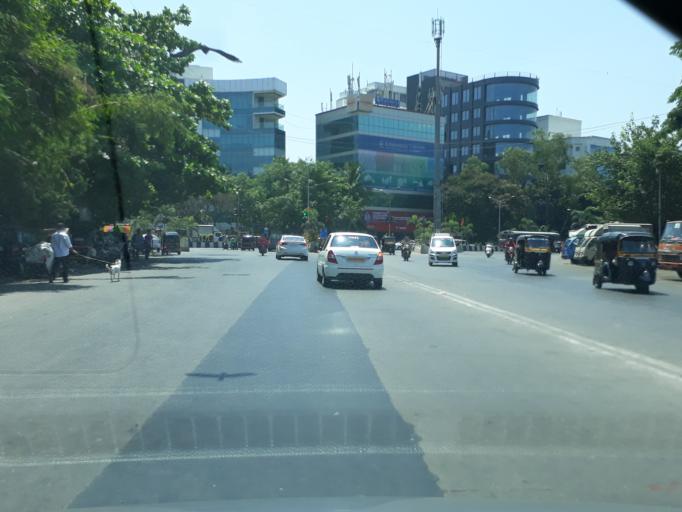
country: IN
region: Maharashtra
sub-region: Mumbai Suburban
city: Mumbai
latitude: 19.0747
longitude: 72.8595
